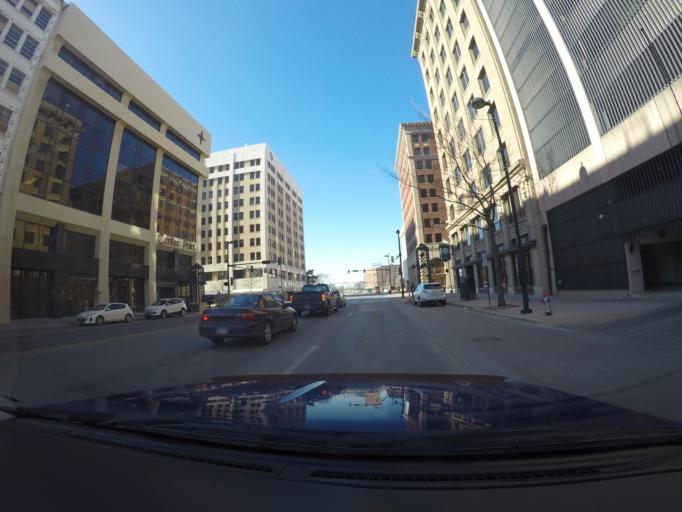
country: US
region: Kansas
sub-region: Sedgwick County
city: Wichita
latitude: 37.6861
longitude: -97.3377
